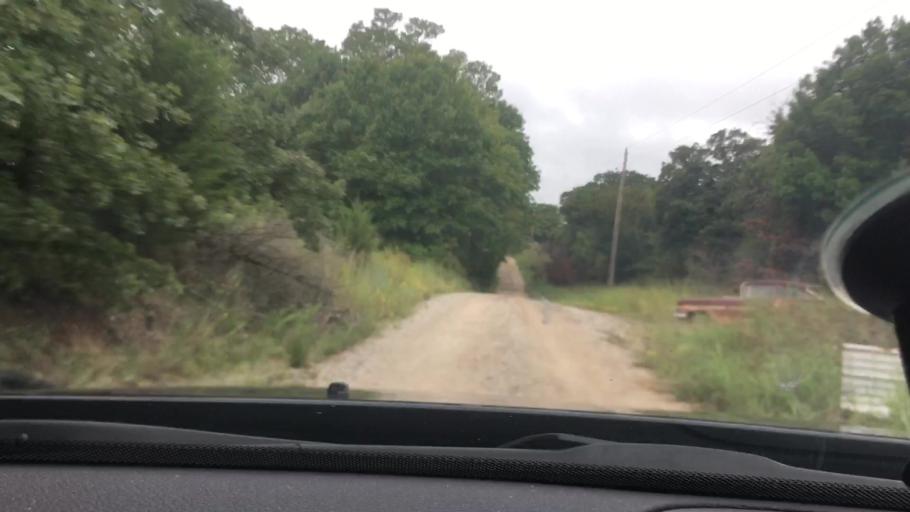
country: US
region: Oklahoma
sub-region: Pontotoc County
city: Ada
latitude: 34.8037
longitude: -96.7485
